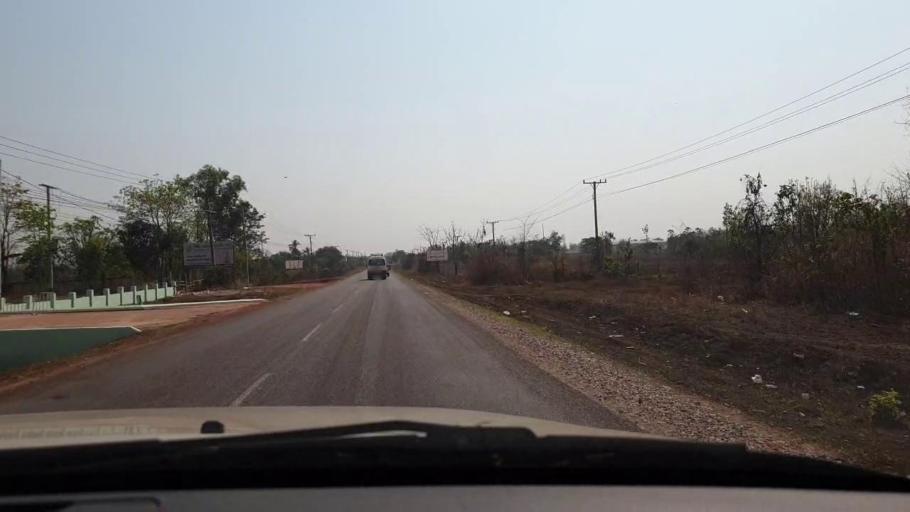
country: TH
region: Nong Khai
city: Nong Khai
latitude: 18.0555
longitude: 102.8300
